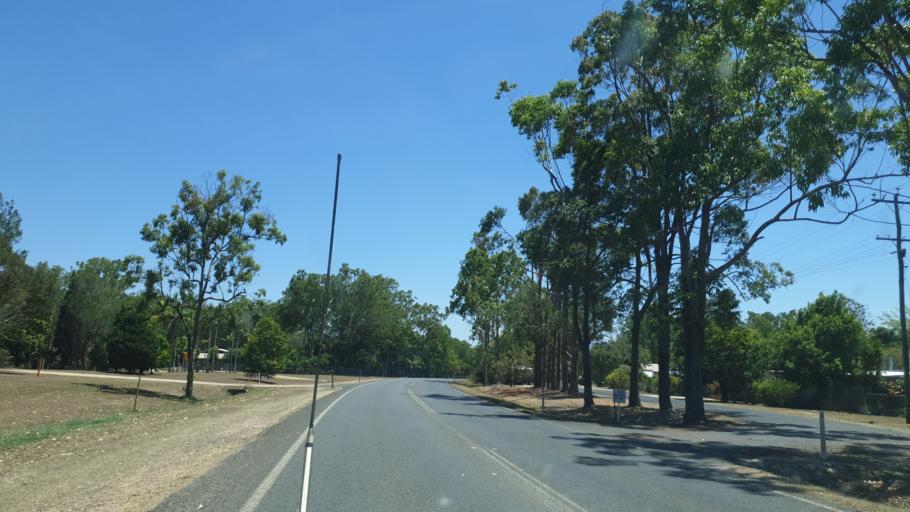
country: AU
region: Queensland
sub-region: Tablelands
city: Atherton
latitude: -17.2808
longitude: 145.4697
